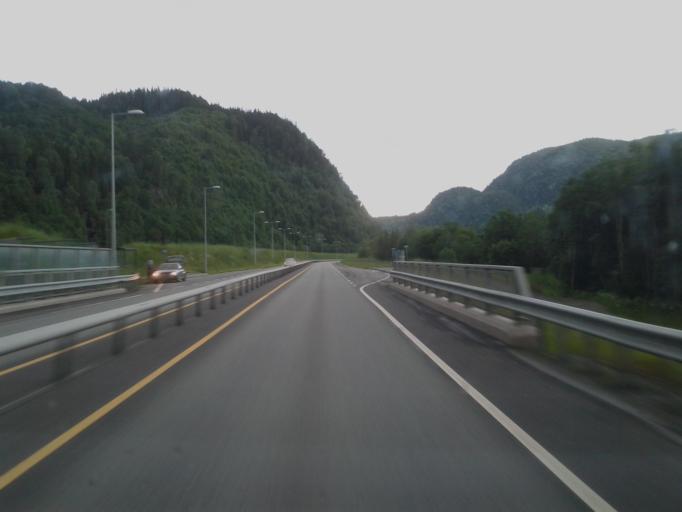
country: NO
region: Sor-Trondelag
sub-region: Midtre Gauldal
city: Storen
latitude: 63.0831
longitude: 10.2533
